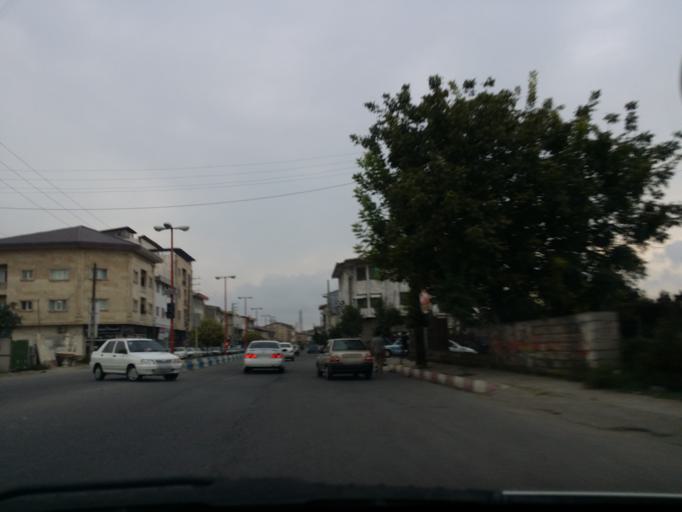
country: IR
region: Mazandaran
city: `Abbasabad
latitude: 36.7222
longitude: 51.1032
